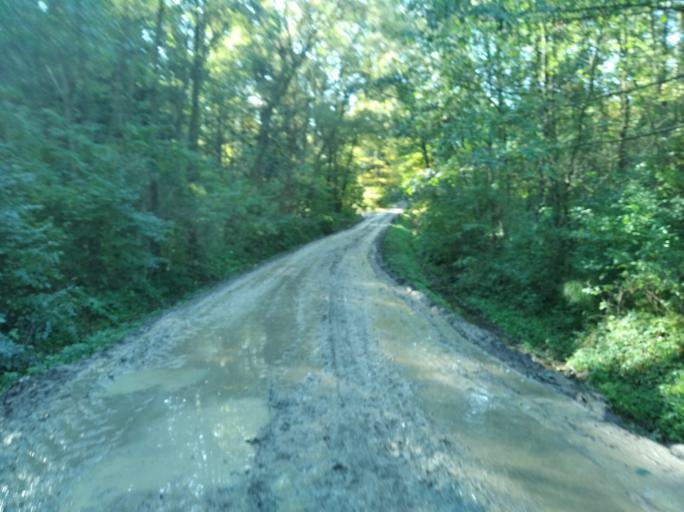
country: PL
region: Subcarpathian Voivodeship
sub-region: Powiat strzyzowski
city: Strzyzow
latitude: 49.8347
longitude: 21.7982
